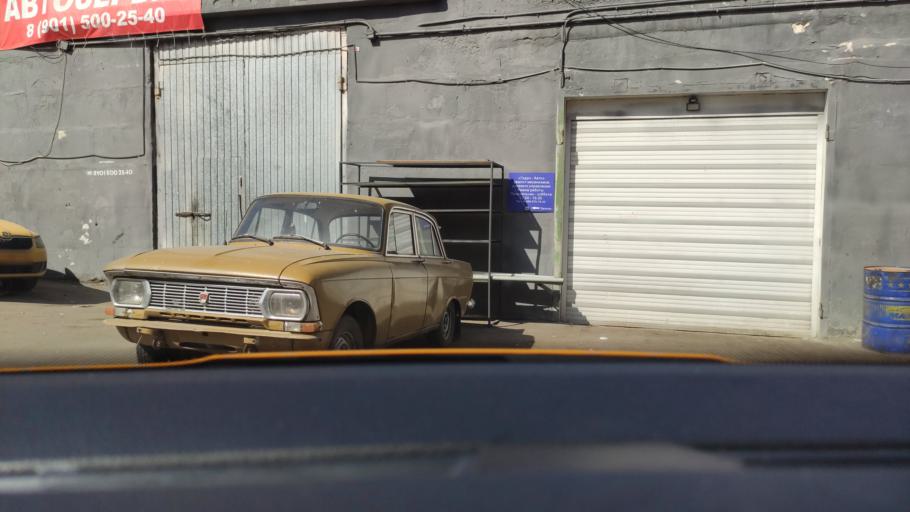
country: RU
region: Moscow
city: Zapadnoye Degunino
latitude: 55.8618
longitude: 37.5473
